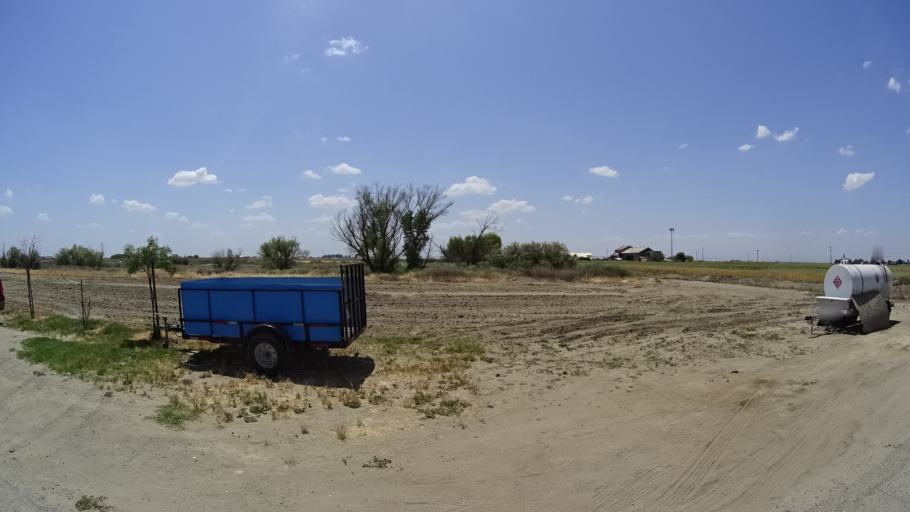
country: US
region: California
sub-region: Kings County
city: Stratford
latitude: 36.1857
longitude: -119.8222
